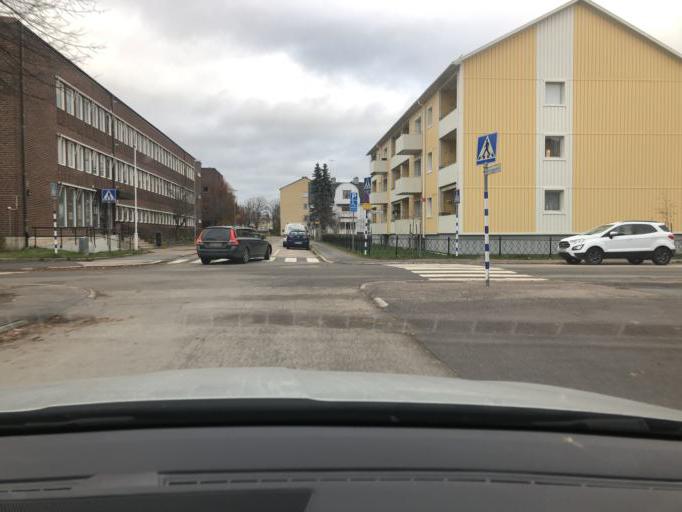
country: SE
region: Uppsala
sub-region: Tierps Kommun
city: Tierp
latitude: 60.3414
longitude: 17.5160
